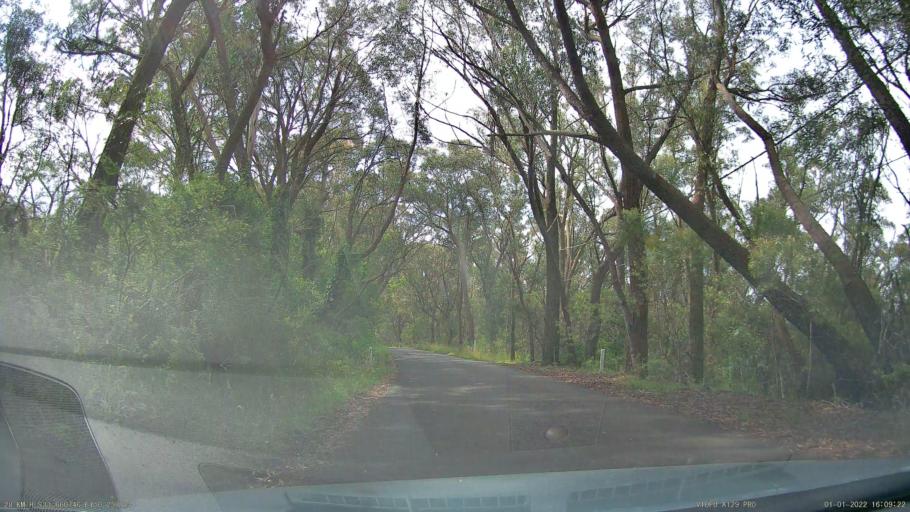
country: AU
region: New South Wales
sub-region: Blue Mountains Municipality
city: Blackheath
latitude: -33.6607
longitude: 150.2587
